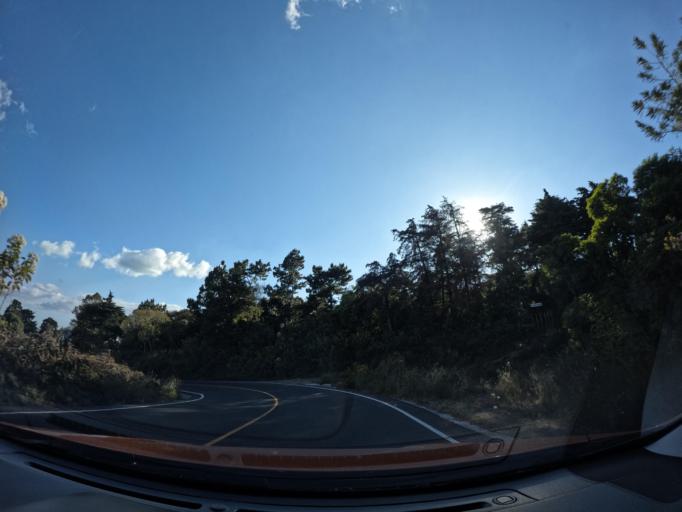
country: GT
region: Escuintla
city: Palin
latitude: 14.4496
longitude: -90.6927
